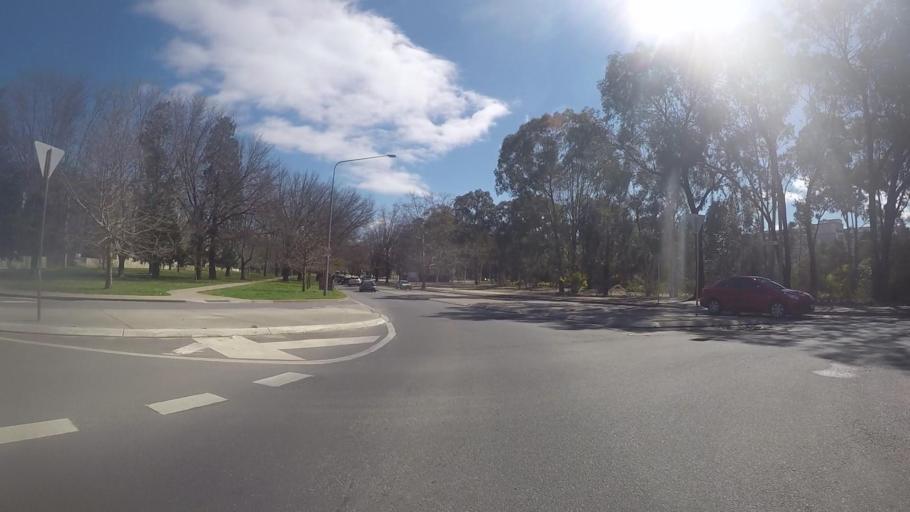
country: AU
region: Australian Capital Territory
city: Forrest
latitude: -35.3023
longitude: 149.1363
